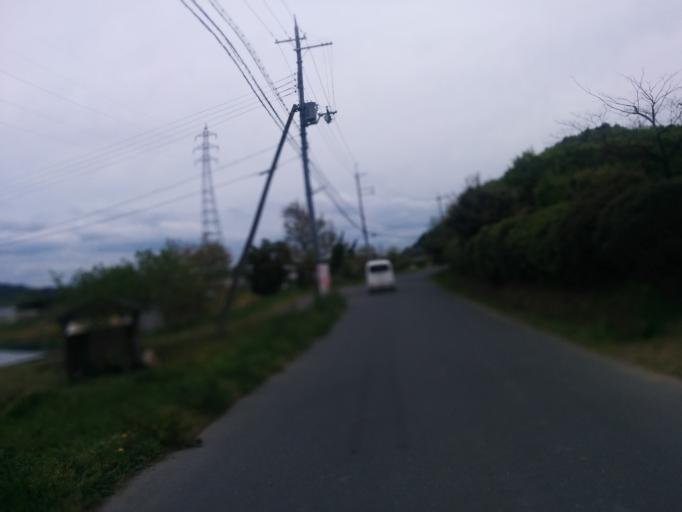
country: JP
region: Kyoto
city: Ayabe
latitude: 35.2053
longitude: 135.4363
